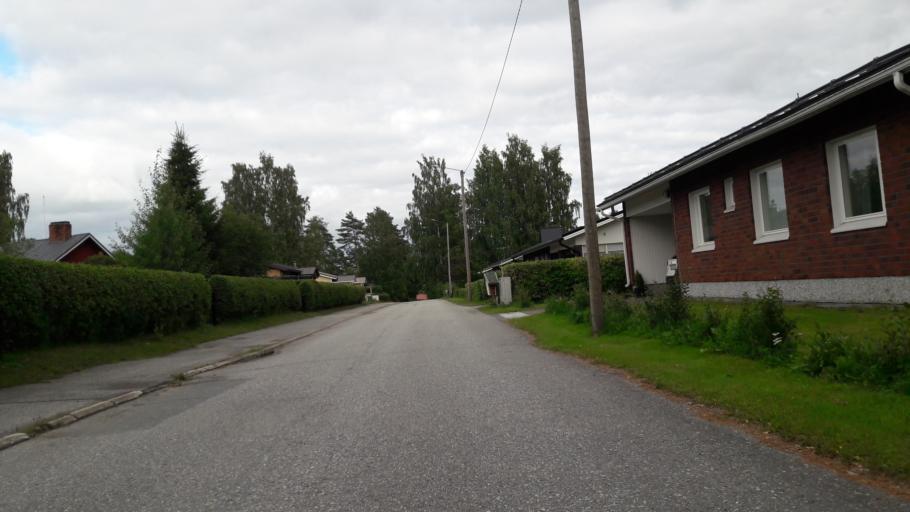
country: FI
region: North Karelia
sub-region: Joensuu
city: Joensuu
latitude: 62.5816
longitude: 29.7993
